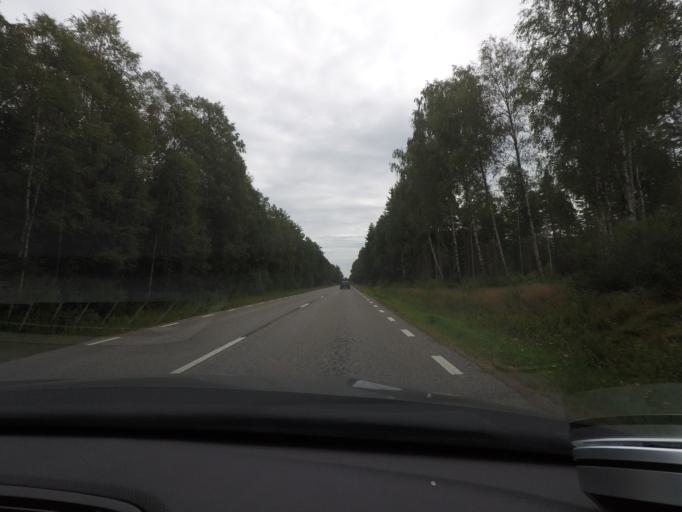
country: SE
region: Blekinge
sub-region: Olofstroms Kommun
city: Olofstroem
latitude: 56.4659
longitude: 14.6499
